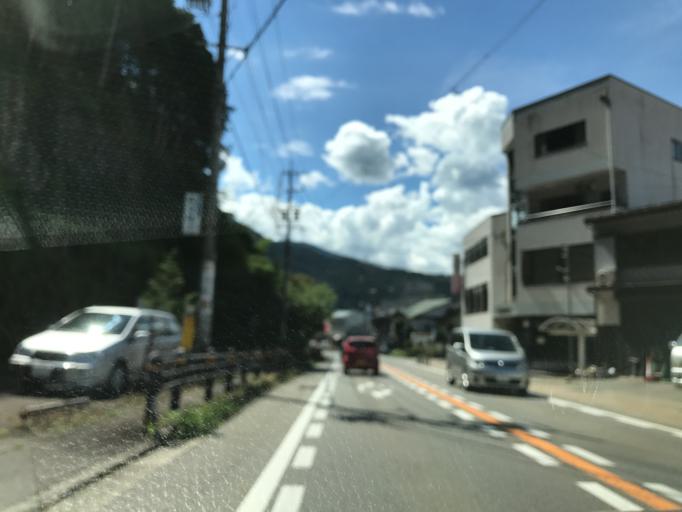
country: JP
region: Gifu
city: Gujo
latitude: 35.7465
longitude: 136.9556
